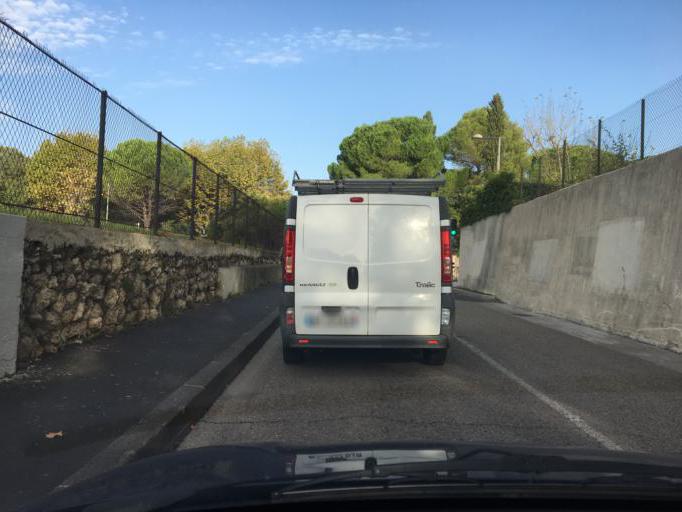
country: FR
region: Languedoc-Roussillon
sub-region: Departement de l'Herault
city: Montpellier
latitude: 43.6201
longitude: 3.8766
